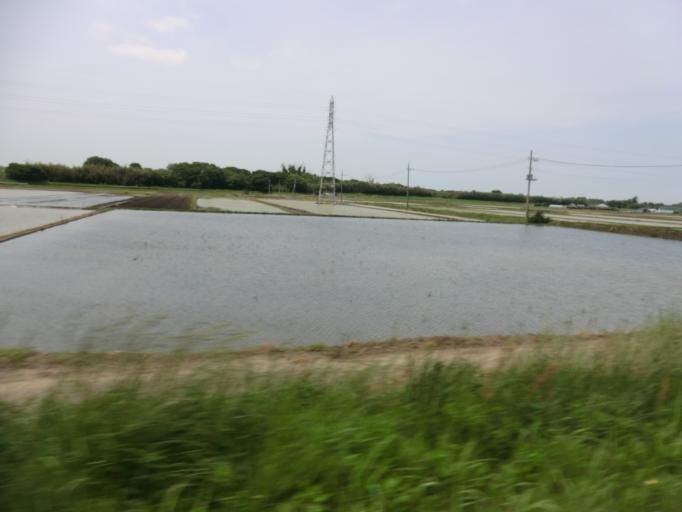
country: JP
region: Ibaraki
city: Tsukuba
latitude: 36.2111
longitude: 140.0711
